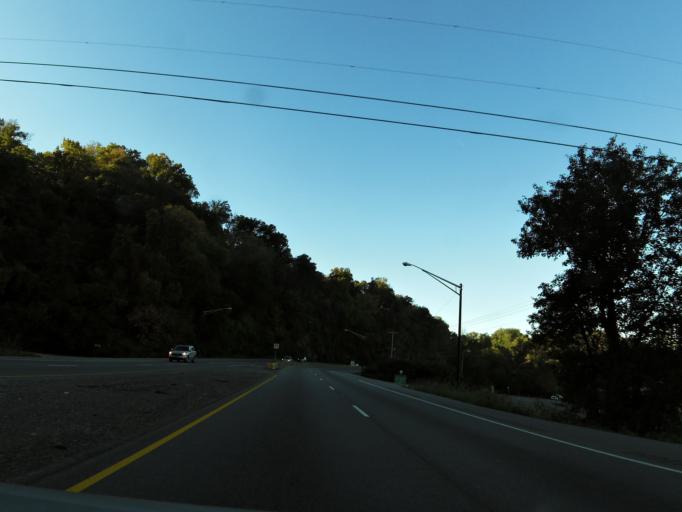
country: US
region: Tennessee
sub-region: Knox County
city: Knoxville
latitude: 35.9300
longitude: -83.9496
